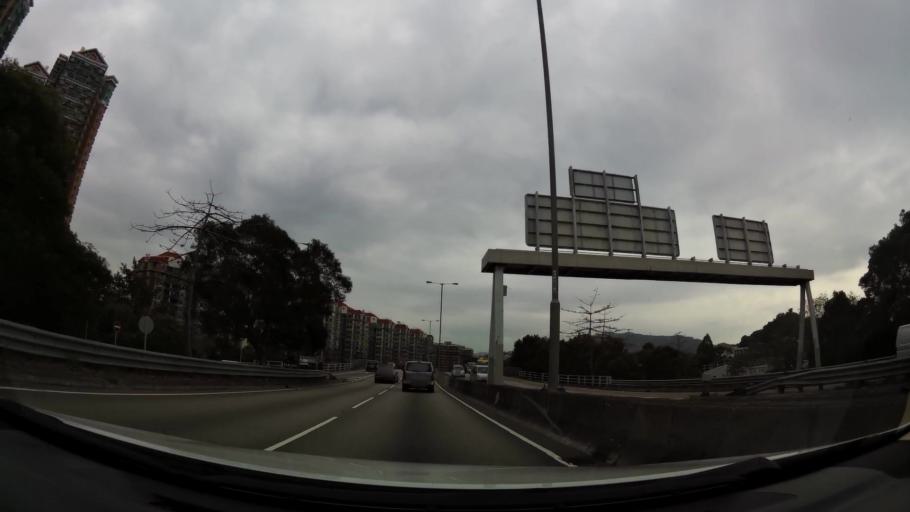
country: HK
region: Yuen Long
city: Yuen Long Kau Hui
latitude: 22.4450
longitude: 114.0167
